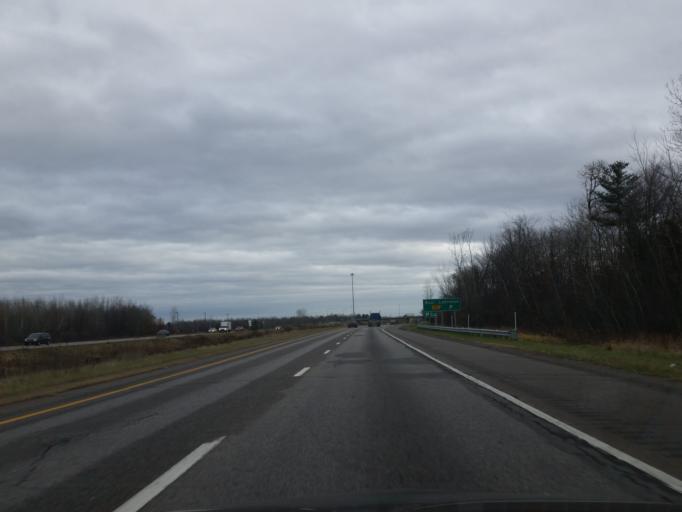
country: CA
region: Quebec
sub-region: Outaouais
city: Gatineau
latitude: 45.5105
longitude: -75.6527
